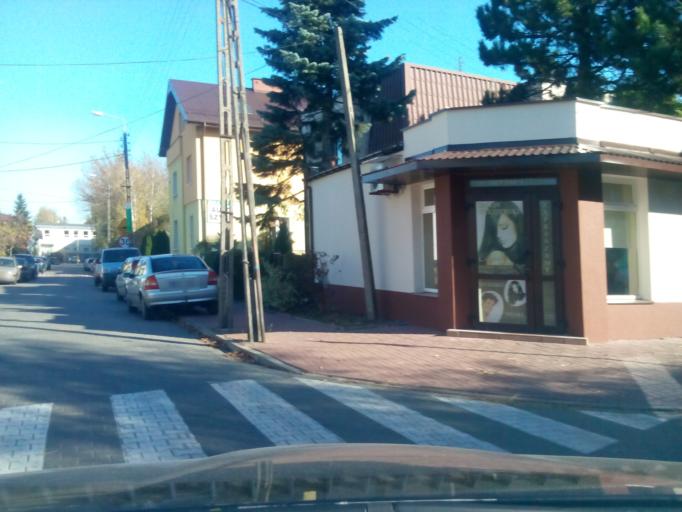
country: PL
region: Masovian Voivodeship
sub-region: Powiat pruszkowski
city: Pruszkow
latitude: 52.1599
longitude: 20.7932
